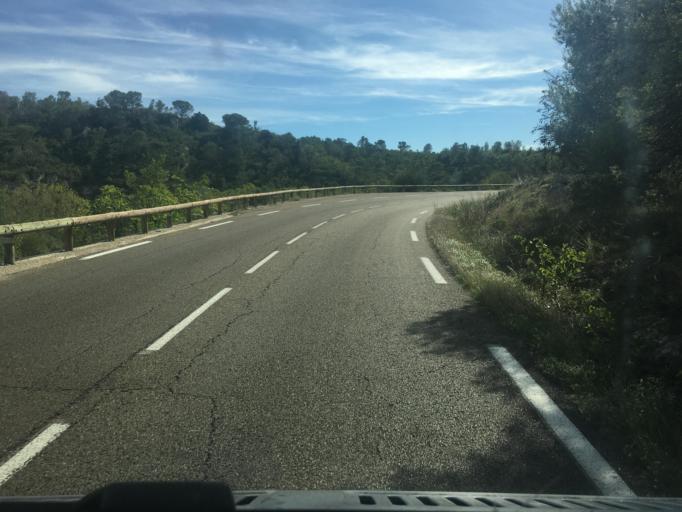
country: FR
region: Languedoc-Roussillon
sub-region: Departement du Gard
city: Uzes
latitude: 44.0164
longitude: 4.4294
